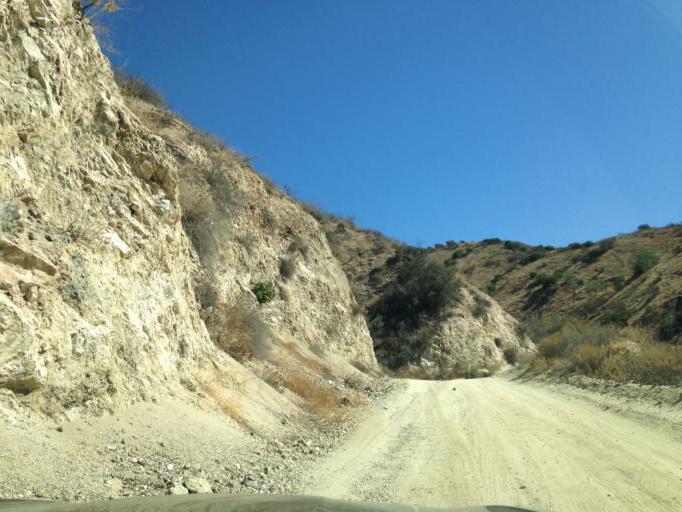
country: US
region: California
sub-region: San Bernardino County
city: Mentone
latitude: 34.1128
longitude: -117.1251
